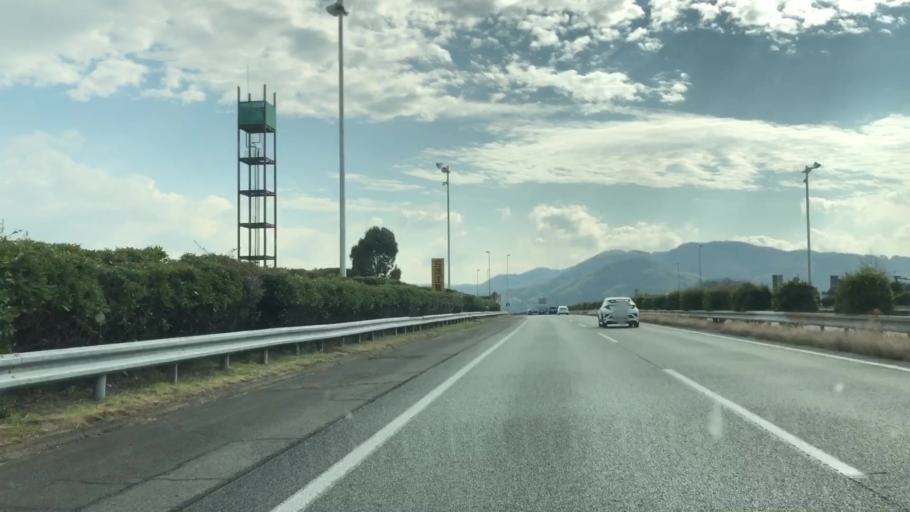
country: JP
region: Fukuoka
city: Setakamachi-takayanagi
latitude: 33.1287
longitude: 130.5177
